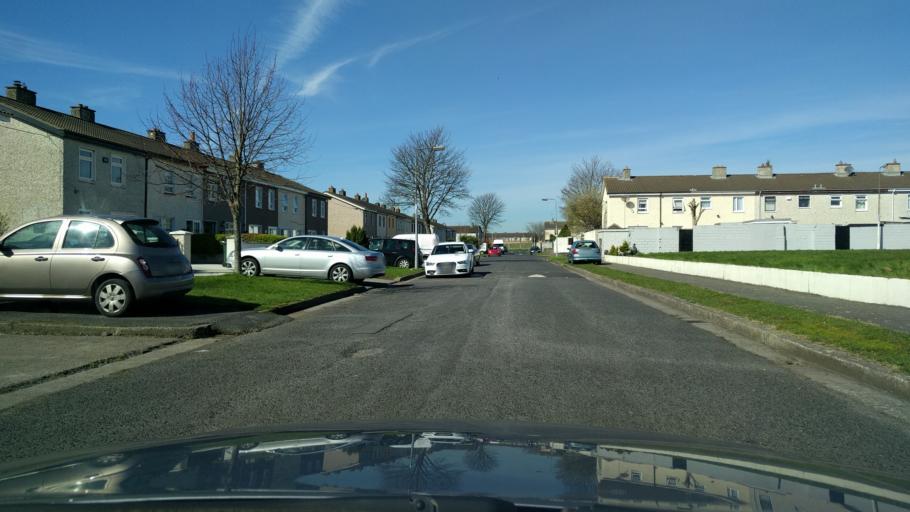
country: IE
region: Leinster
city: Tallaght
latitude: 53.2785
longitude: -6.3879
